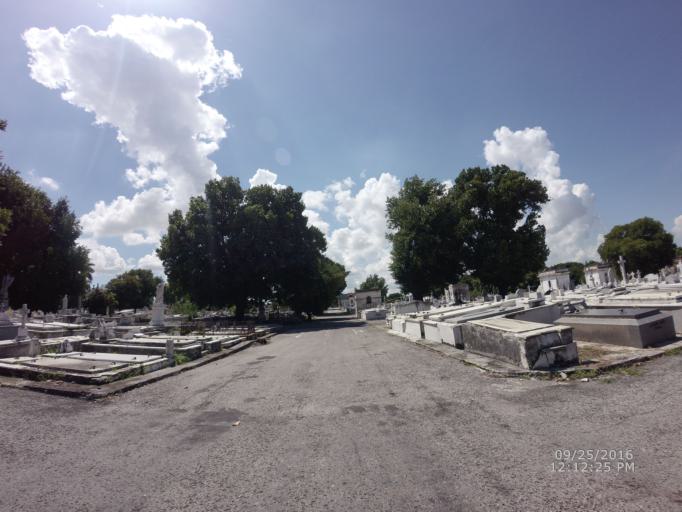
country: CU
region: La Habana
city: Havana
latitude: 23.1247
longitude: -82.3957
